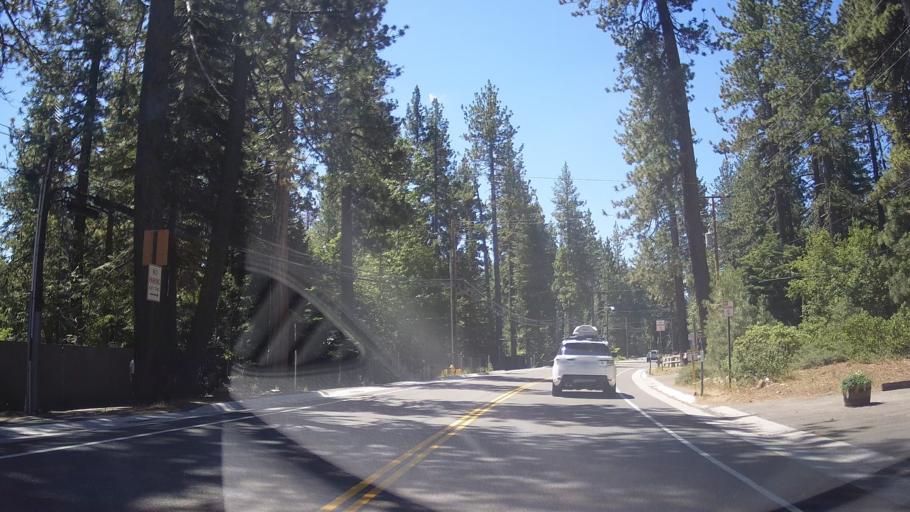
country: US
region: California
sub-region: Placer County
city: Sunnyside-Tahoe City
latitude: 39.1387
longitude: -120.1541
